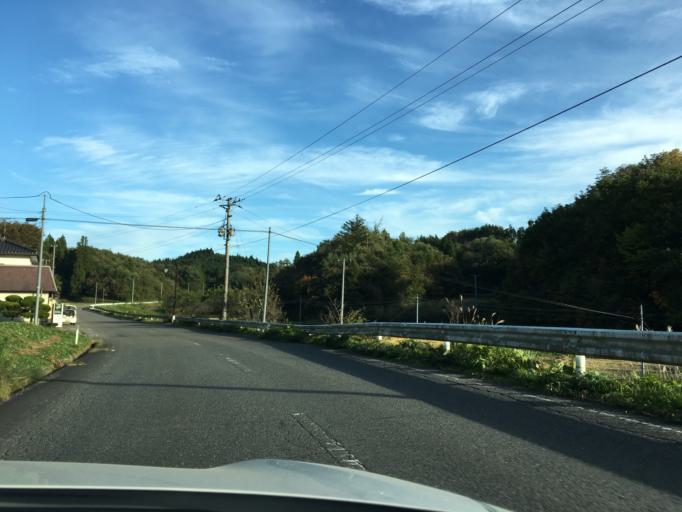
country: JP
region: Fukushima
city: Ishikawa
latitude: 37.1896
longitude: 140.5430
